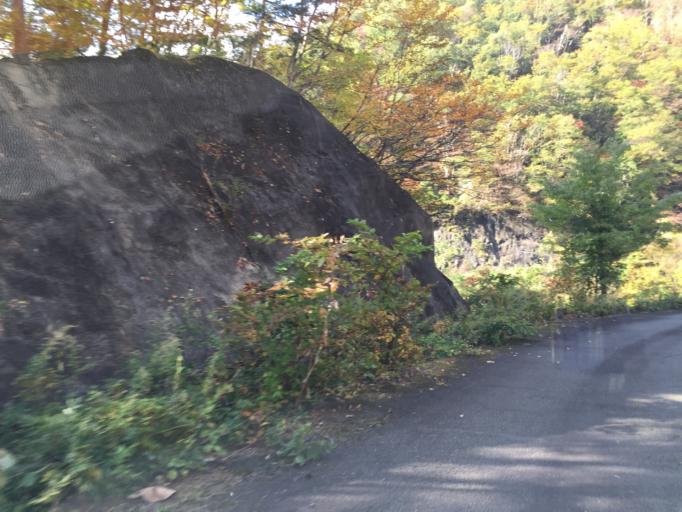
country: JP
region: Fukushima
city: Kitakata
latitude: 37.7479
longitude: 139.9262
